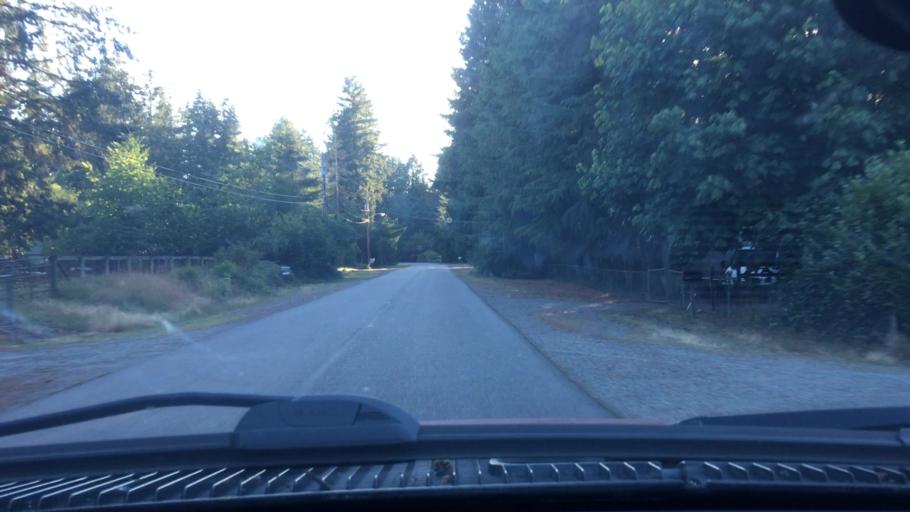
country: US
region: Washington
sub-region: King County
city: Lake Morton-Berrydale
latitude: 47.3473
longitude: -122.0785
